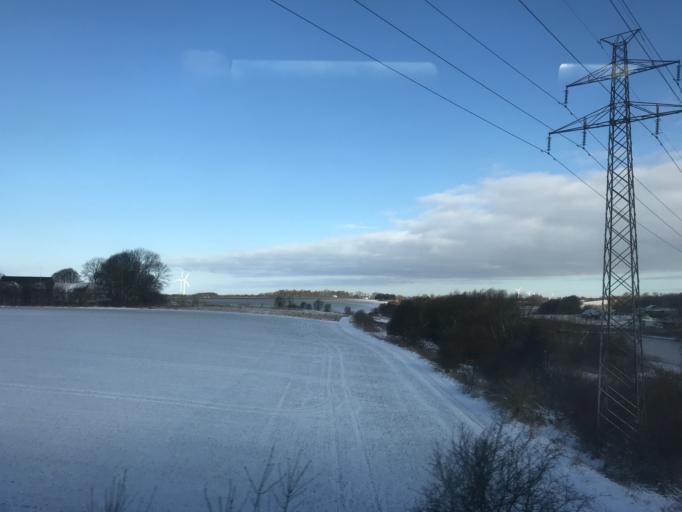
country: SE
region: Skane
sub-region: Staffanstorps Kommun
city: Hjaerup
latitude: 55.6900
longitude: 13.1634
